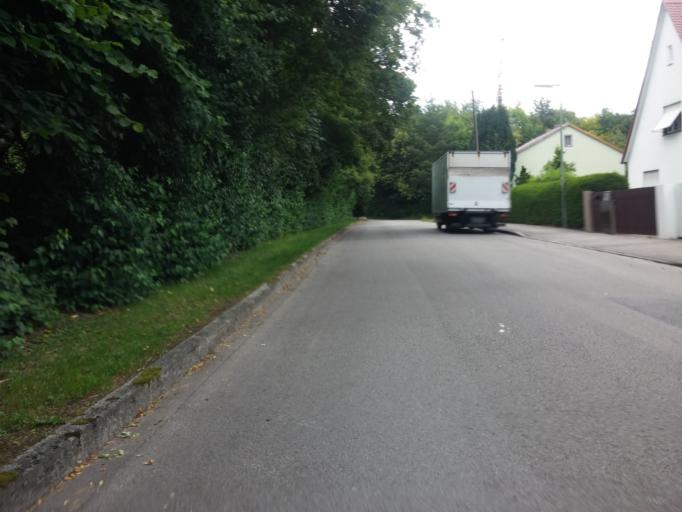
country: DE
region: Bavaria
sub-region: Upper Bavaria
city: Bogenhausen
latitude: 48.1598
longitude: 11.6375
